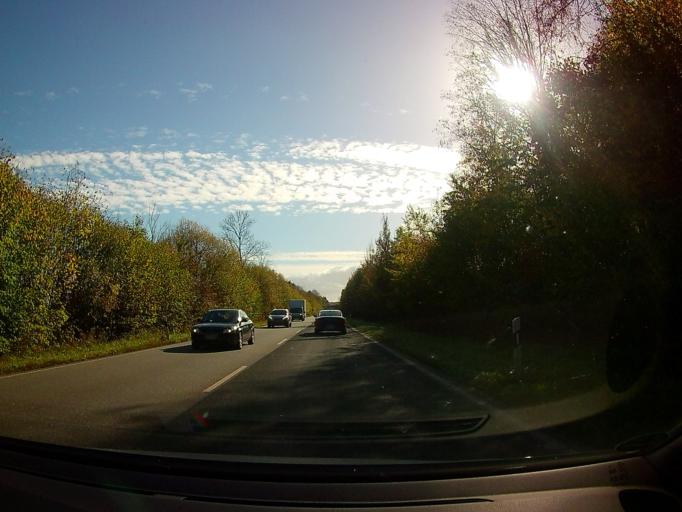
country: DE
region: Schleswig-Holstein
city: Todendorf
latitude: 53.6949
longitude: 10.3733
